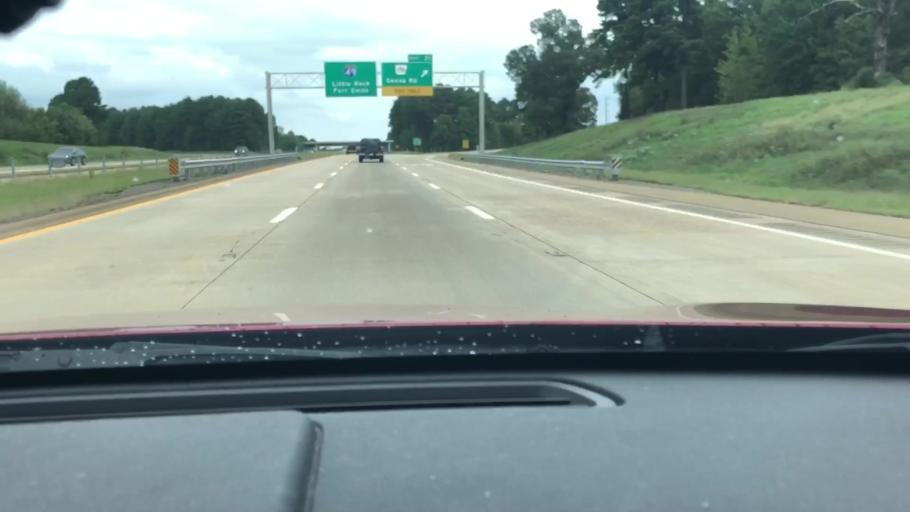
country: US
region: Texas
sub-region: Bowie County
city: Texarkana
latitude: 33.4064
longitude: -94.0048
